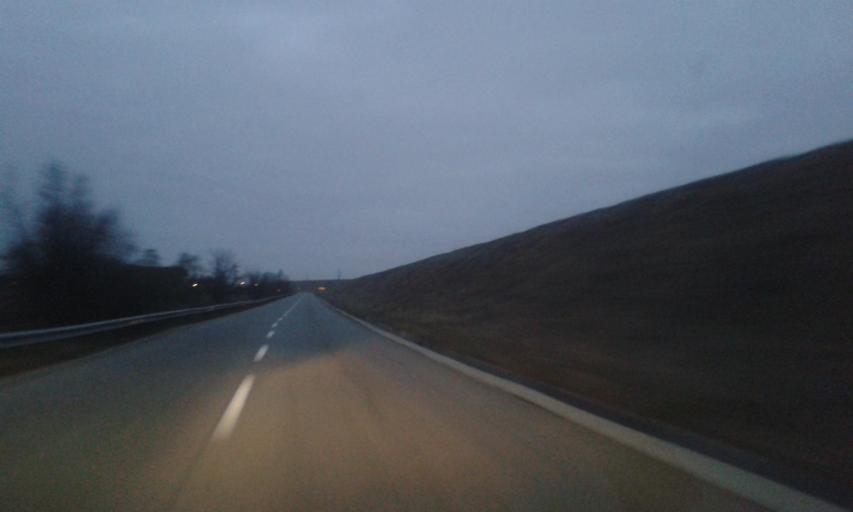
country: RO
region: Gorj
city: Targu Jiu
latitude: 45.0650
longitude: 23.2763
